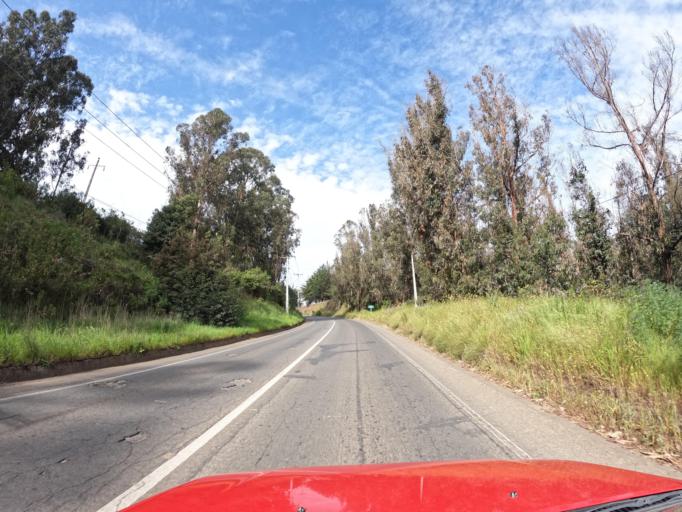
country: CL
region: O'Higgins
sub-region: Provincia de Colchagua
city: Santa Cruz
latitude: -34.3824
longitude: -71.9760
